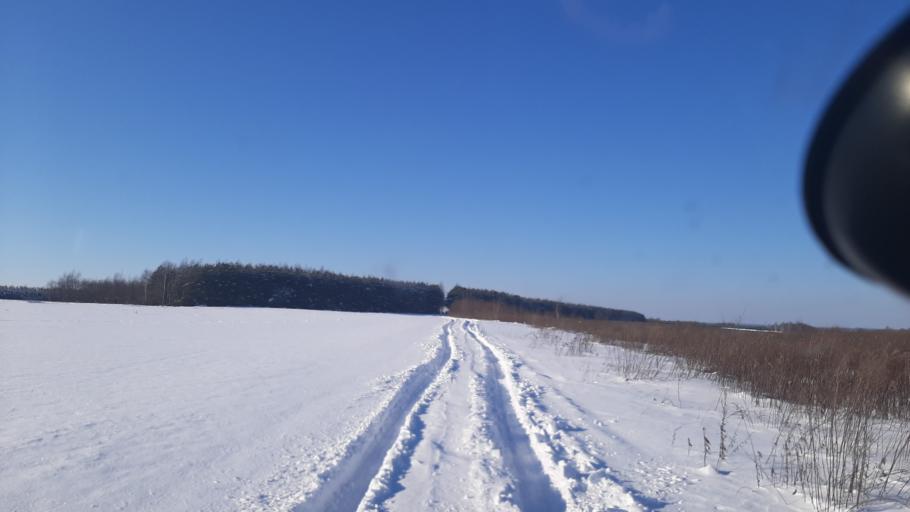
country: PL
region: Lublin Voivodeship
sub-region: Powiat lubelski
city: Jastkow
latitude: 51.3750
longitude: 22.4418
